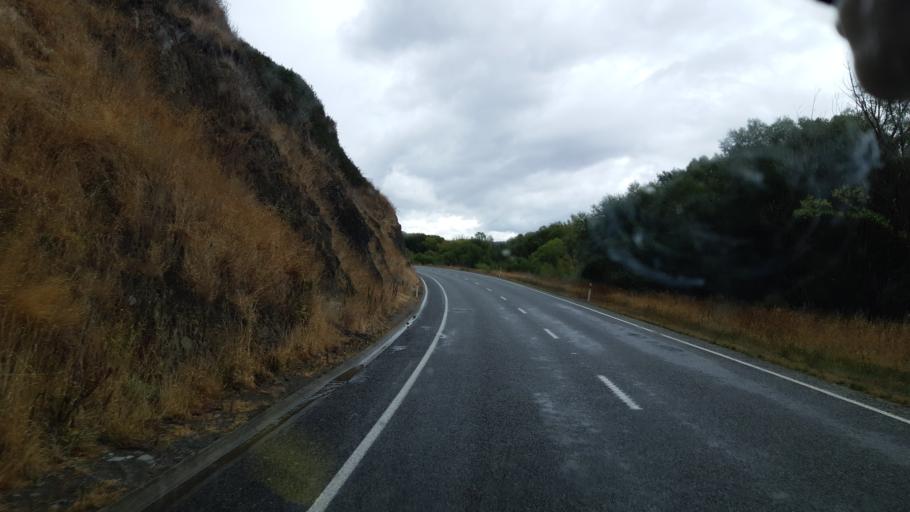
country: NZ
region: Canterbury
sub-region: Hurunui District
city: Amberley
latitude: -42.5785
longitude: 172.7534
